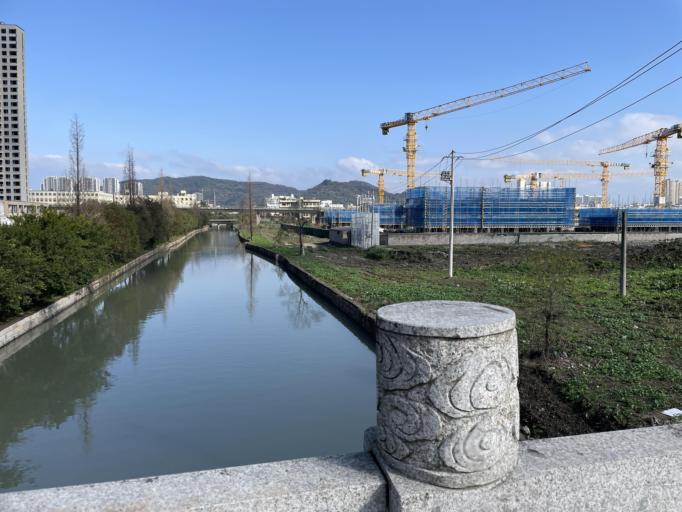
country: CN
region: Zhejiang Sheng
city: Louqiao
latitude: 27.9777
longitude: 120.6195
